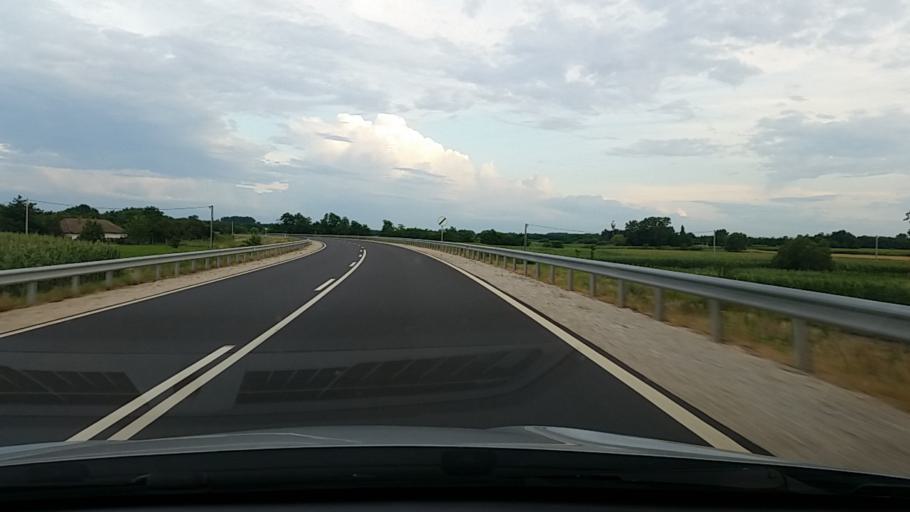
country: HU
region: Szabolcs-Szatmar-Bereg
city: Kalmanhaza
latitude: 47.9240
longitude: 21.6430
